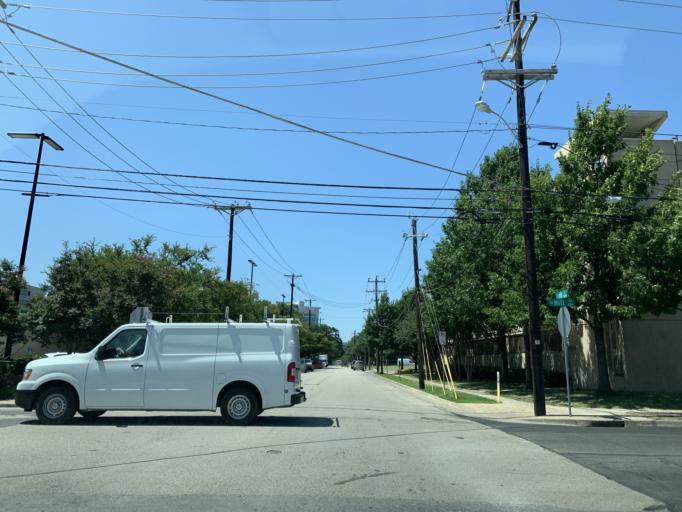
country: US
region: Texas
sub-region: Dallas County
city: Dallas
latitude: 32.7913
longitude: -96.7758
